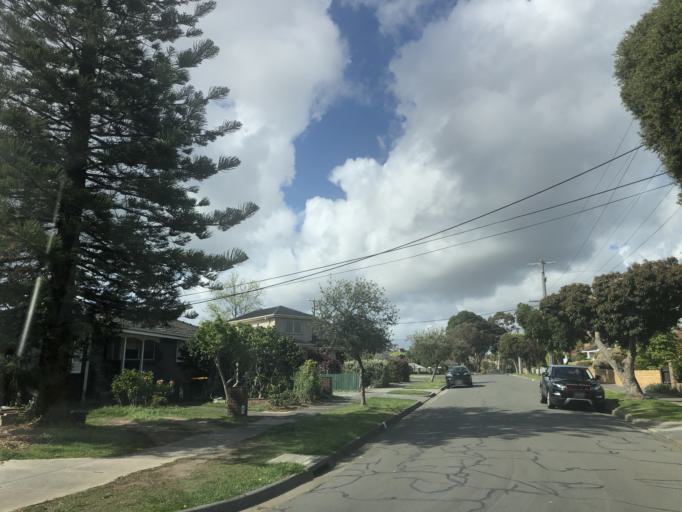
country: AU
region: Victoria
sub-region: Monash
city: Ashwood
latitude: -37.8773
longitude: 145.1193
